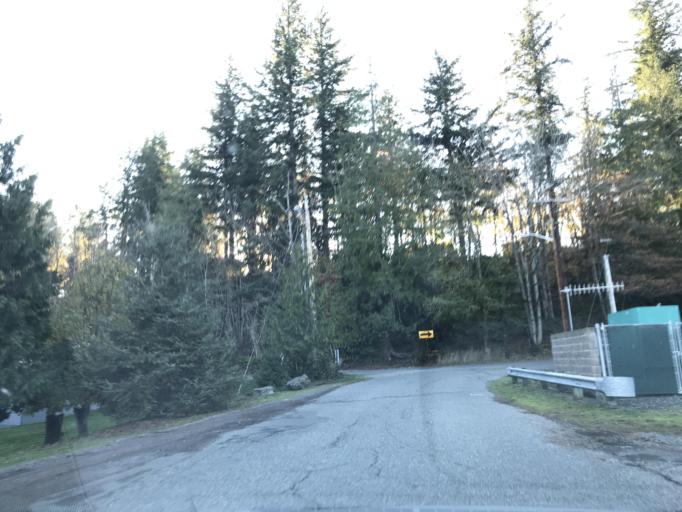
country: US
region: Washington
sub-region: Whatcom County
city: Geneva
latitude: 48.7546
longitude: -122.4188
